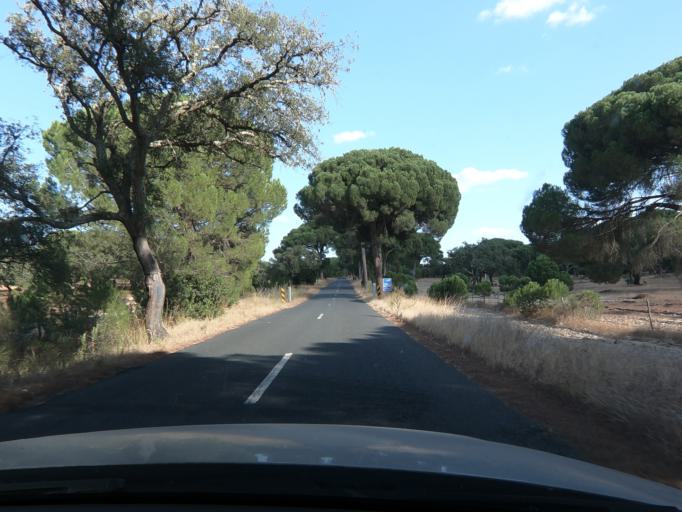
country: PT
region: Setubal
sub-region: Alcacer do Sal
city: Alcacer do Sal
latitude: 38.2644
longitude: -8.3411
